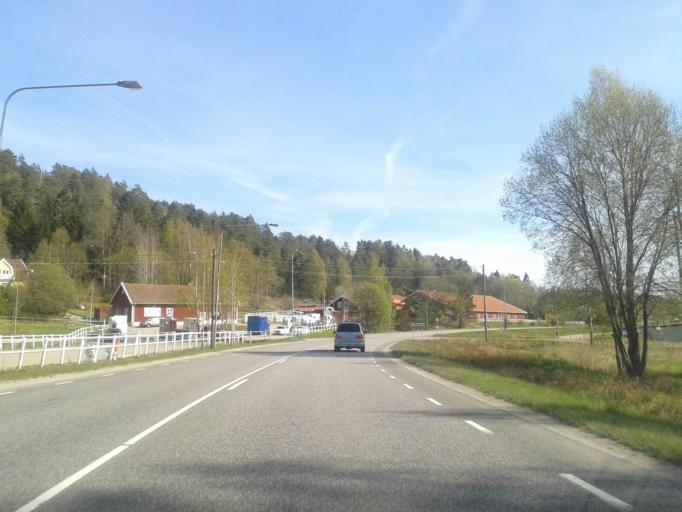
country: SE
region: Vaestra Goetaland
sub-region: Ale Kommun
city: Nodinge-Nol
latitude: 57.8960
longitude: 12.0670
